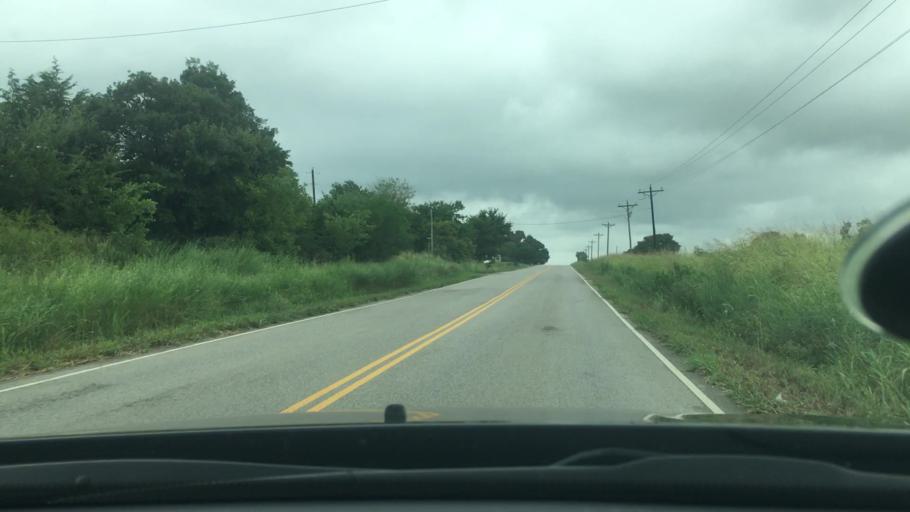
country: US
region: Oklahoma
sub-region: Bryan County
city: Calera
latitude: 33.9474
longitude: -96.5005
